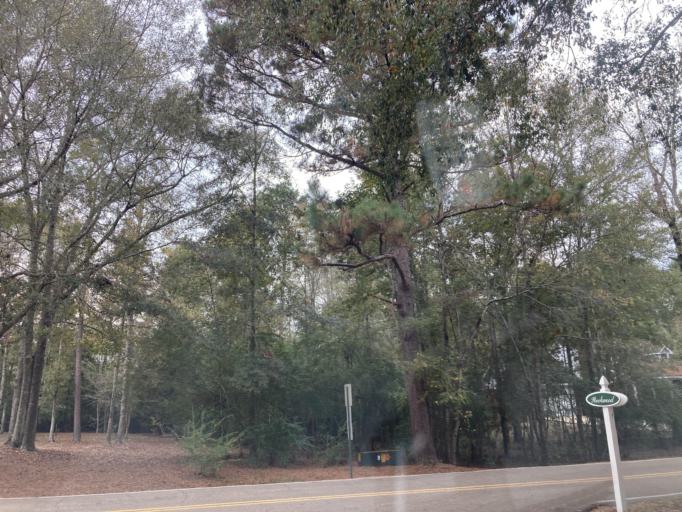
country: US
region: Mississippi
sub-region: Lamar County
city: West Hattiesburg
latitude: 31.3095
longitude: -89.4671
